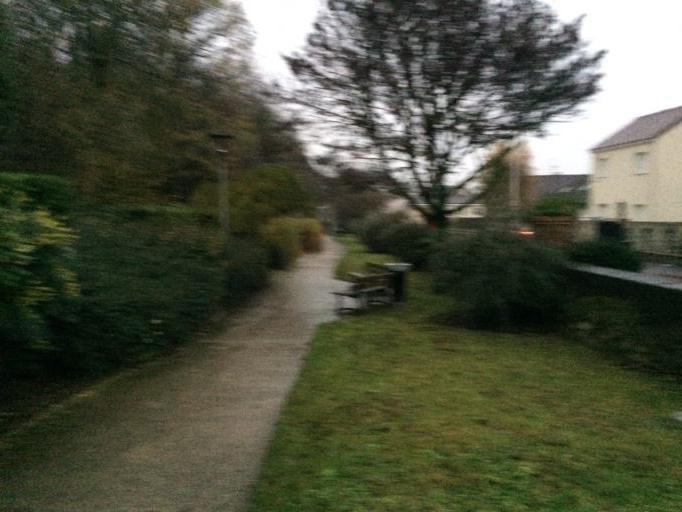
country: FR
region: Ile-de-France
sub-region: Departement de l'Essonne
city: Athis-Mons
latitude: 48.7069
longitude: 2.3837
